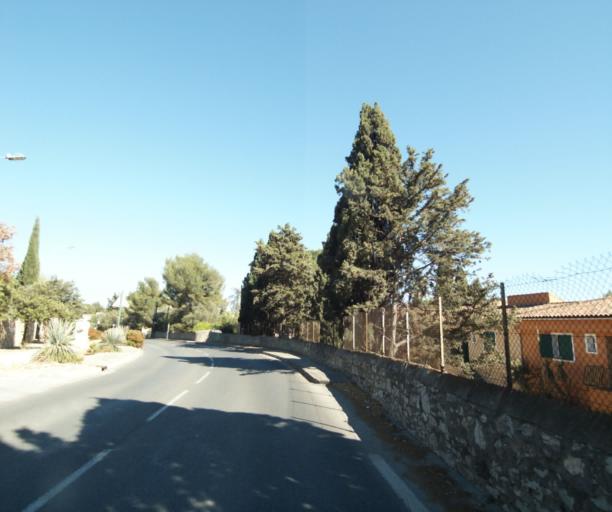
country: FR
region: Provence-Alpes-Cote d'Azur
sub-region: Departement du Var
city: La Garde
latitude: 43.1082
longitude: 5.9829
